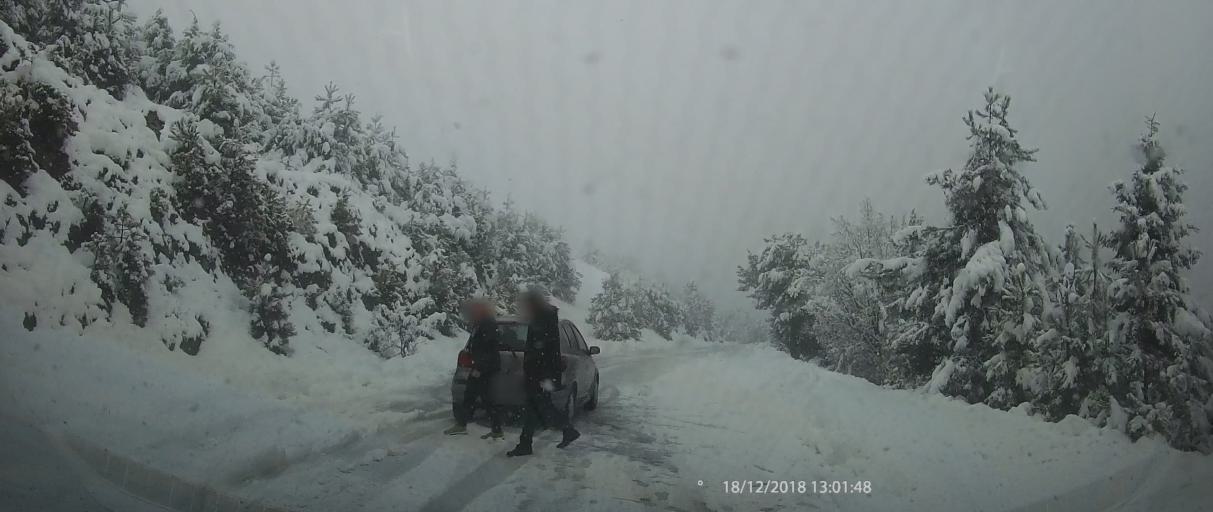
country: GR
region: Central Macedonia
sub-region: Nomos Pierias
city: Litochoro
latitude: 40.1117
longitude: 22.4664
